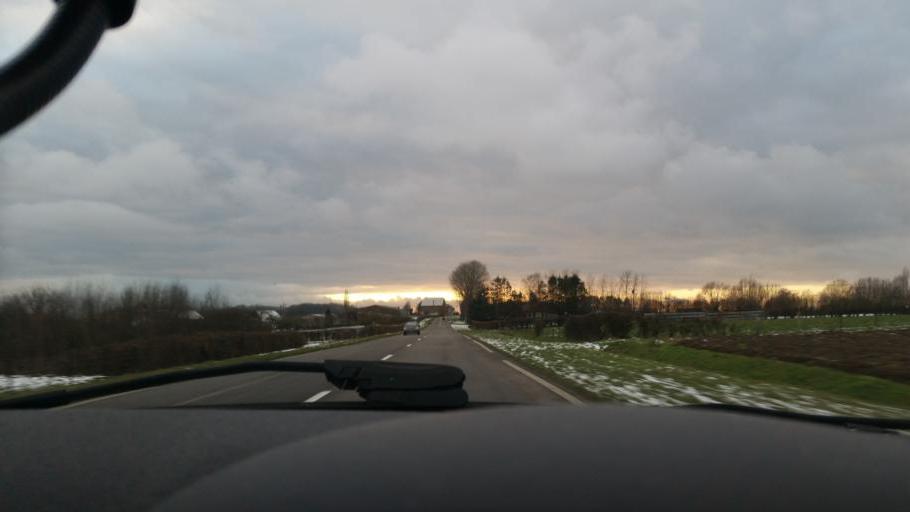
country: FR
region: Nord-Pas-de-Calais
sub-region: Departement du Nord
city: Jeumont
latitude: 50.2507
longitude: 4.1095
